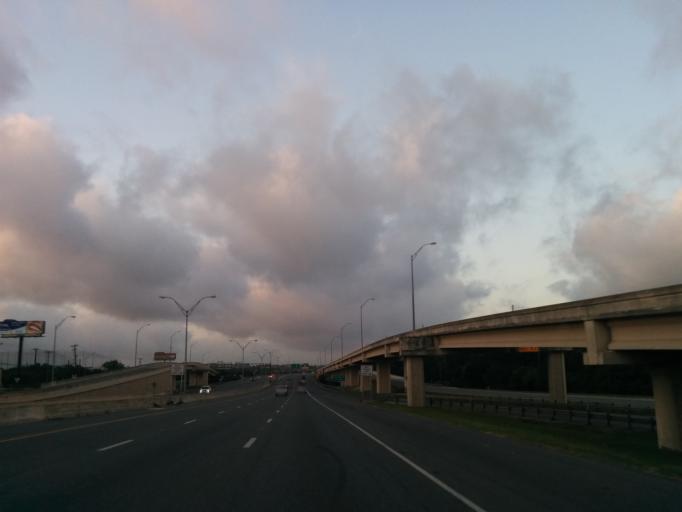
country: US
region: Texas
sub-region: Bexar County
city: Shavano Park
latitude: 29.6033
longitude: -98.6014
